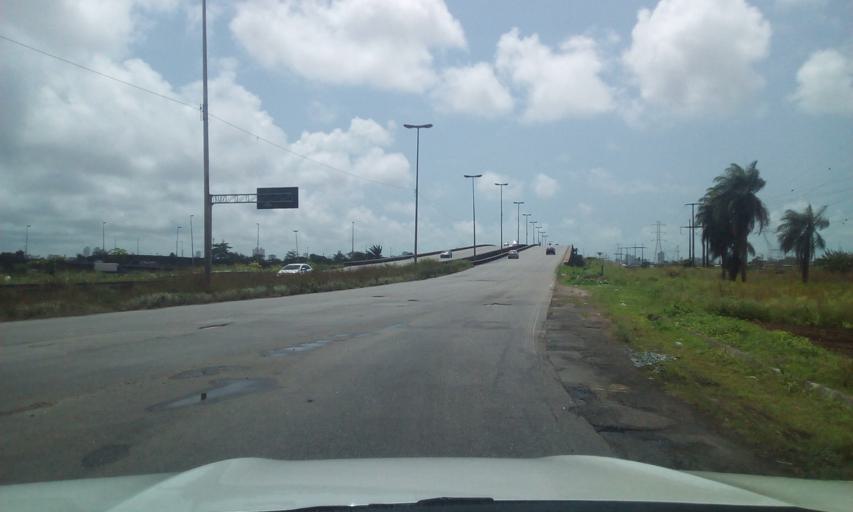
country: BR
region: Pernambuco
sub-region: Recife
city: Recife
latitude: -8.0681
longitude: -34.9452
